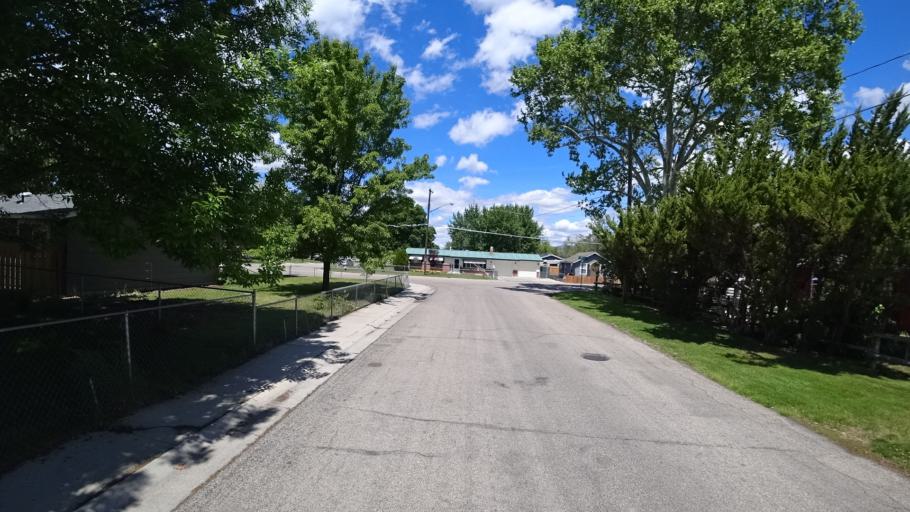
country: US
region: Idaho
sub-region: Ada County
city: Boise
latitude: 43.5787
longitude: -116.2014
